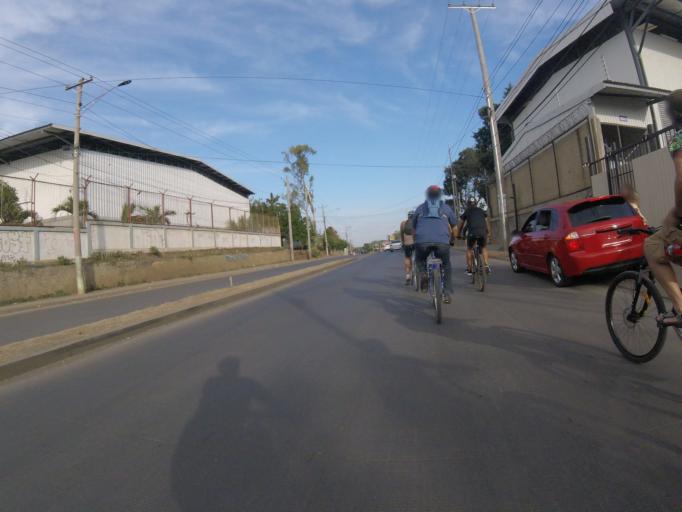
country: NI
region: Managua
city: Managua
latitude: 12.1250
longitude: -86.2024
